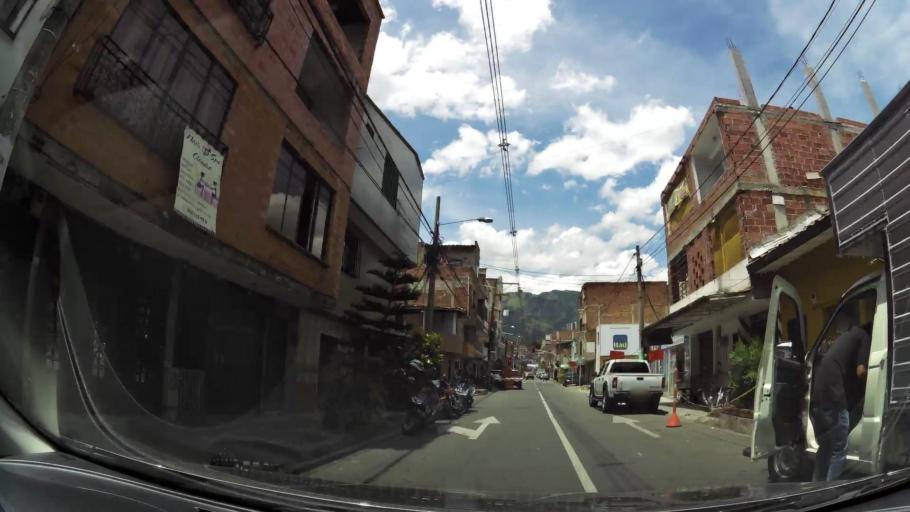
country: CO
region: Antioquia
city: Bello
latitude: 6.3374
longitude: -75.5544
